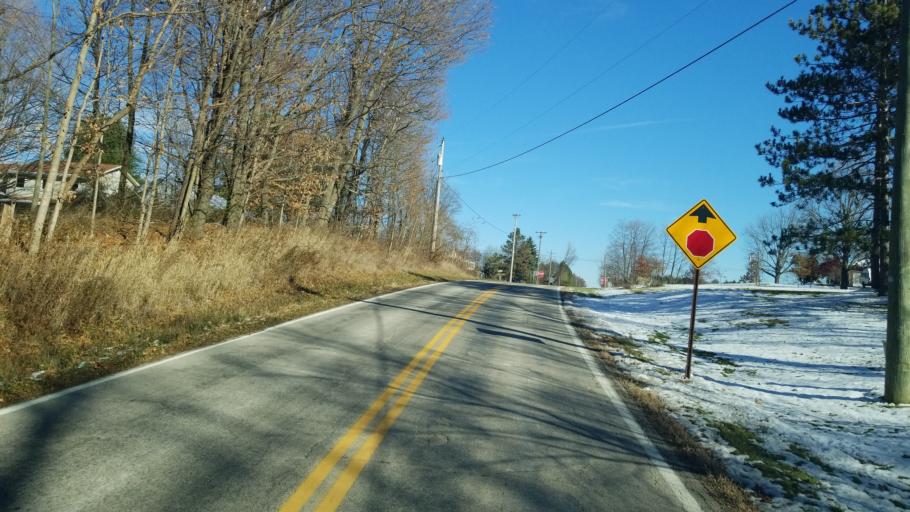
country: US
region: Ohio
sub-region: Richland County
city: Ontario
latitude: 40.7295
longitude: -82.5902
